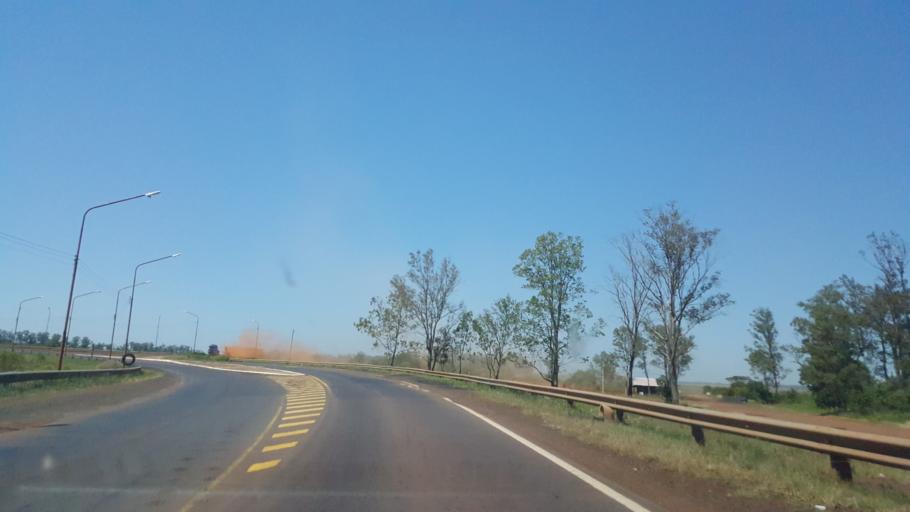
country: AR
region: Corrientes
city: Santo Tome
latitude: -28.3581
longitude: -56.1136
